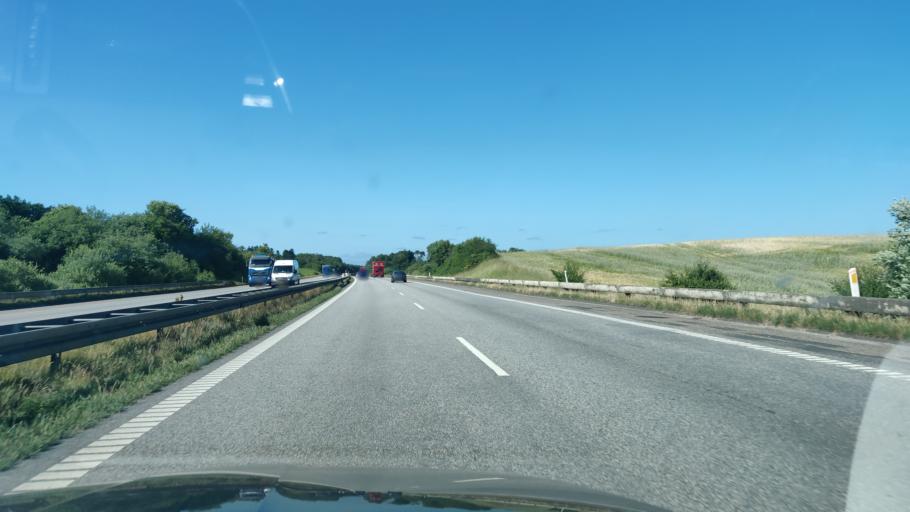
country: DK
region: North Denmark
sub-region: Rebild Kommune
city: Stovring
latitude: 56.9115
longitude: 9.8401
